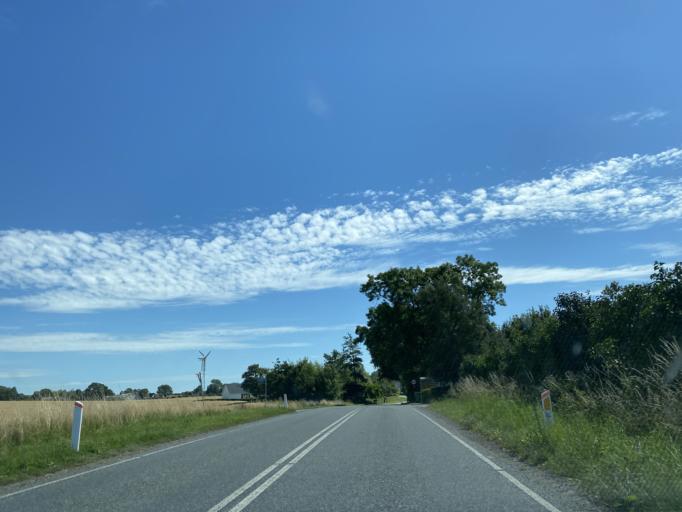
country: DK
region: South Denmark
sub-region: Faaborg-Midtfyn Kommune
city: Ringe
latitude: 55.2094
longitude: 10.3772
